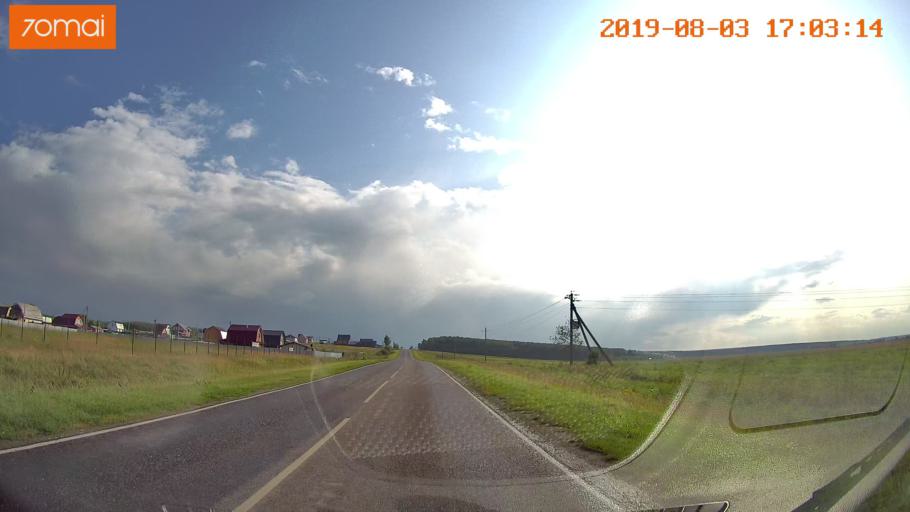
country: RU
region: Moskovskaya
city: Troitskoye
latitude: 55.3400
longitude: 38.5754
